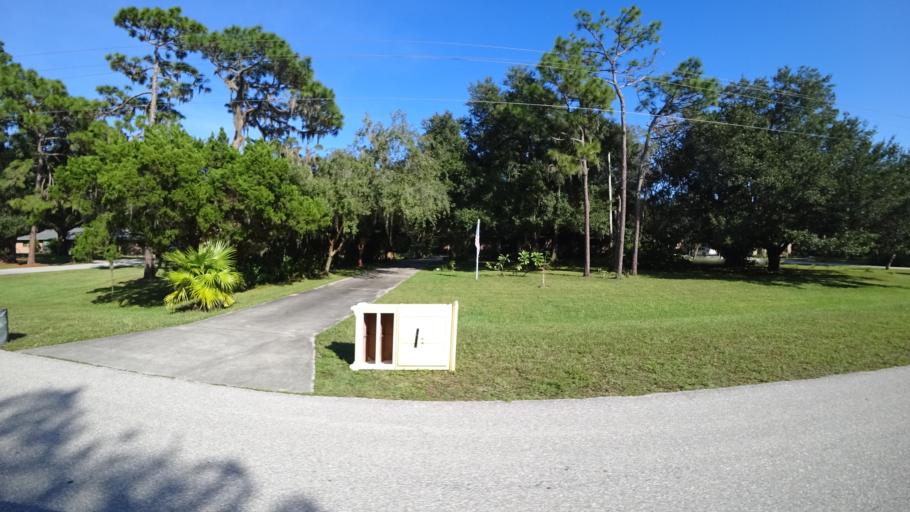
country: US
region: Florida
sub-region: Sarasota County
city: The Meadows
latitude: 27.4211
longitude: -82.4478
